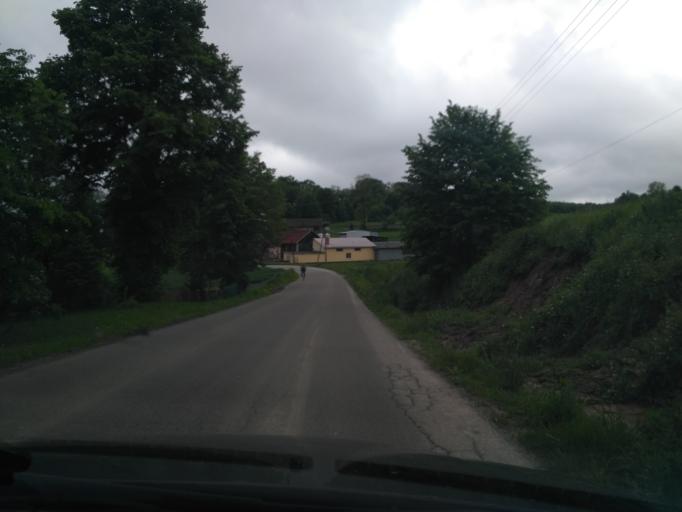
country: PL
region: Subcarpathian Voivodeship
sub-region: Powiat strzyzowski
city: Frysztak
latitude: 49.8046
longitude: 21.5593
